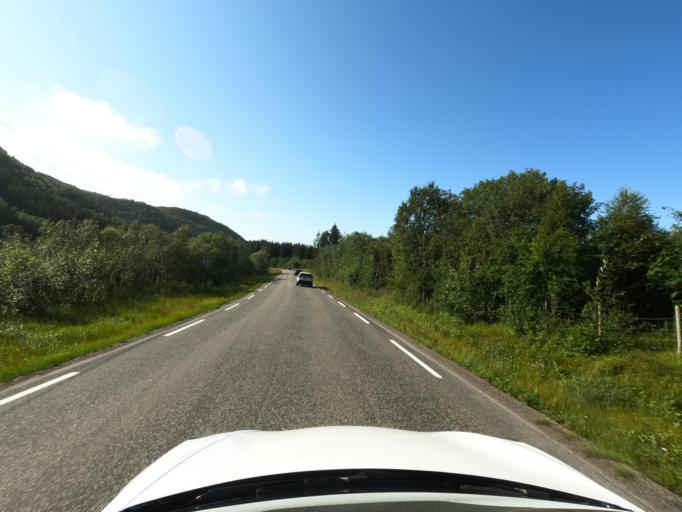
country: NO
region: Nordland
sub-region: Vestvagoy
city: Evjen
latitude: 68.2839
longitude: 13.9029
